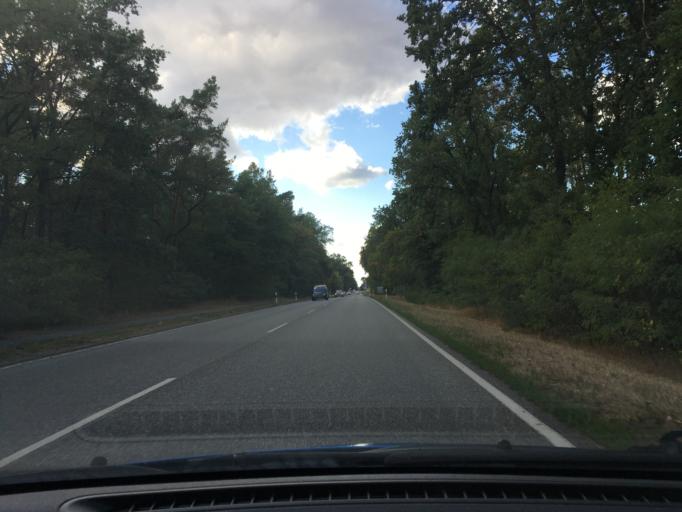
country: DE
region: Mecklenburg-Vorpommern
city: Ludwigslust
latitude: 53.3130
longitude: 11.5108
